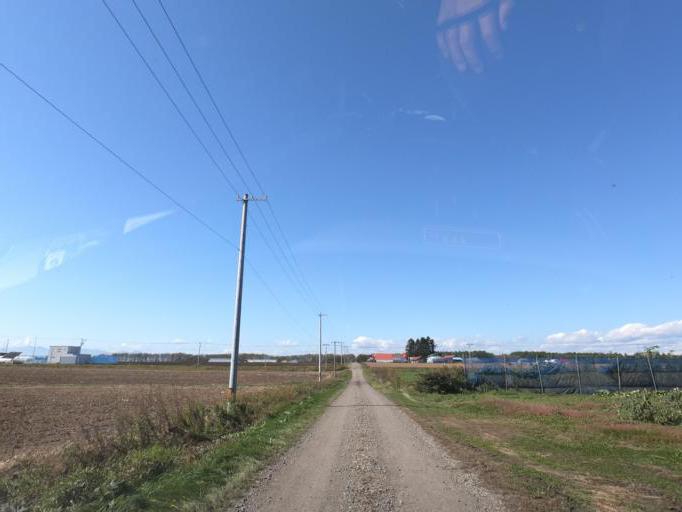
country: JP
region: Hokkaido
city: Otofuke
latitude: 43.0649
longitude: 143.2730
